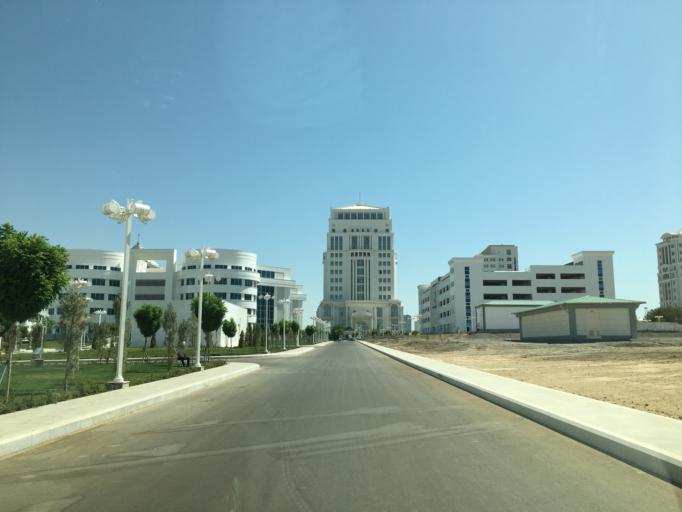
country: TM
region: Ahal
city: Ashgabat
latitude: 37.8919
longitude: 58.3731
